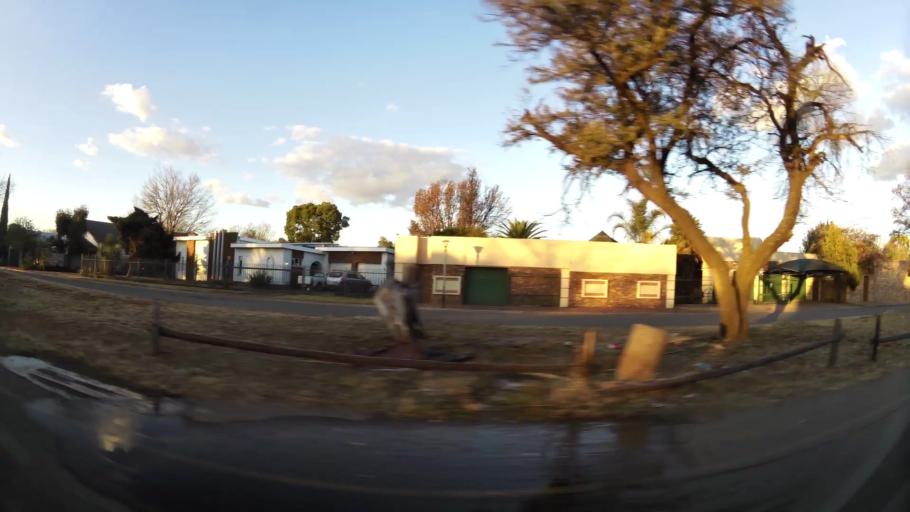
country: ZA
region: North-West
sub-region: Dr Kenneth Kaunda District Municipality
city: Potchefstroom
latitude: -26.7197
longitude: 27.1145
